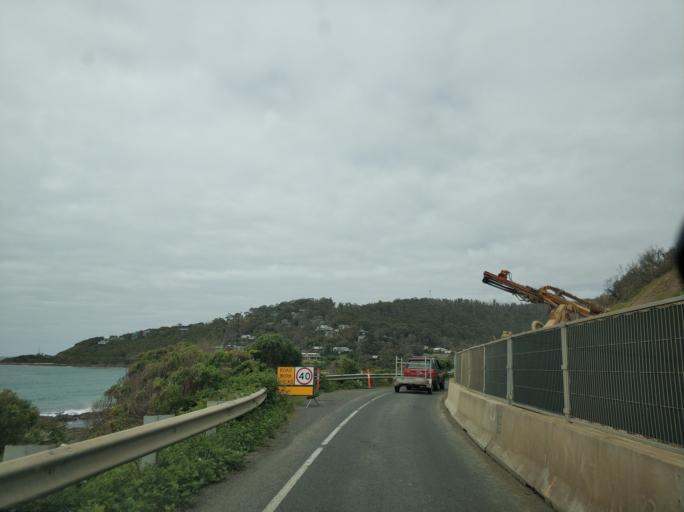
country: AU
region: Victoria
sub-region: Colac-Otway
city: Apollo Bay
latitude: -38.6327
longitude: 143.8959
